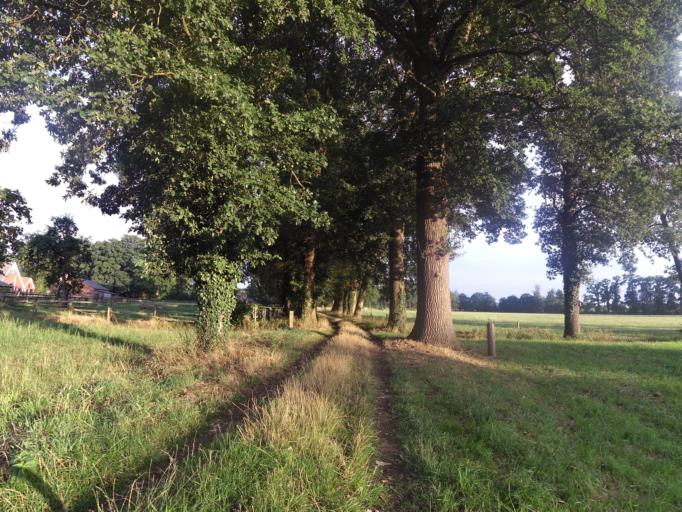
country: NL
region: Gelderland
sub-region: Oude IJsselstreek
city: Varsseveld
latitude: 51.9056
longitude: 6.4810
